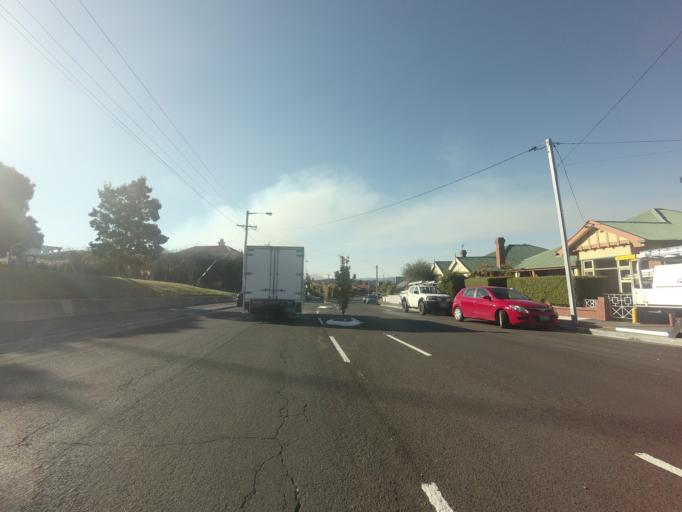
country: AU
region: Tasmania
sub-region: Hobart
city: Hobart
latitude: -42.8811
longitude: 147.3098
